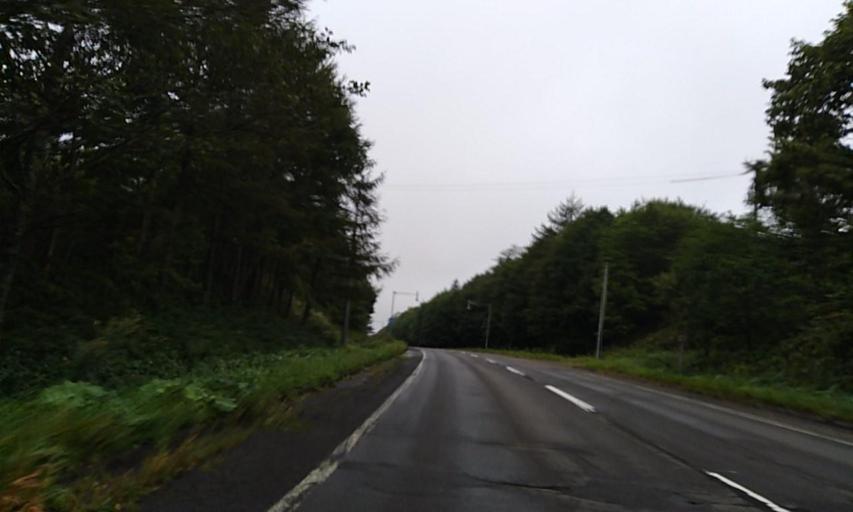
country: JP
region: Hokkaido
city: Kushiro
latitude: 43.4819
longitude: 144.5532
